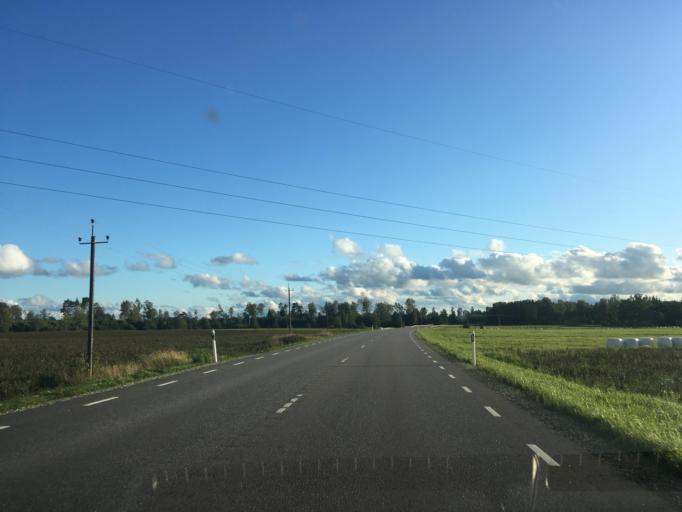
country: EE
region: Raplamaa
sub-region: Maerjamaa vald
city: Marjamaa
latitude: 58.9113
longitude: 24.2881
